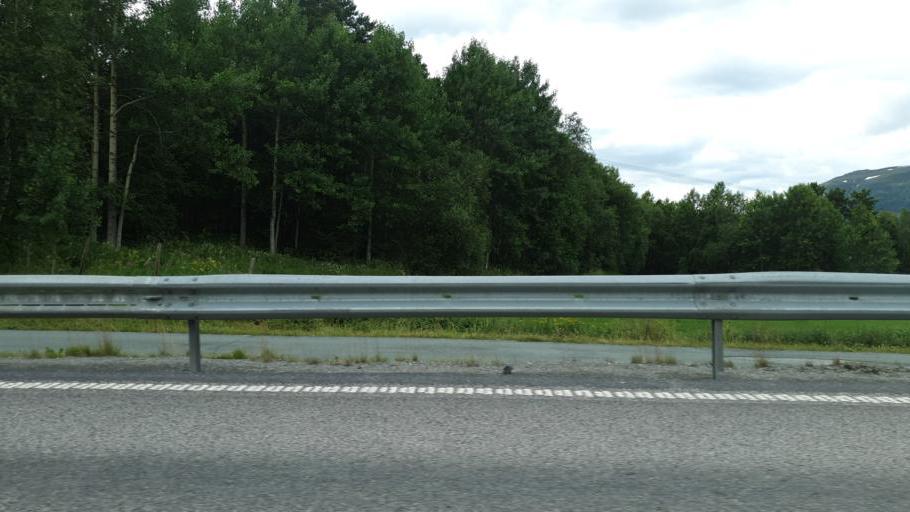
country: NO
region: Sor-Trondelag
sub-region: Oppdal
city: Oppdal
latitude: 62.5780
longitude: 9.6567
